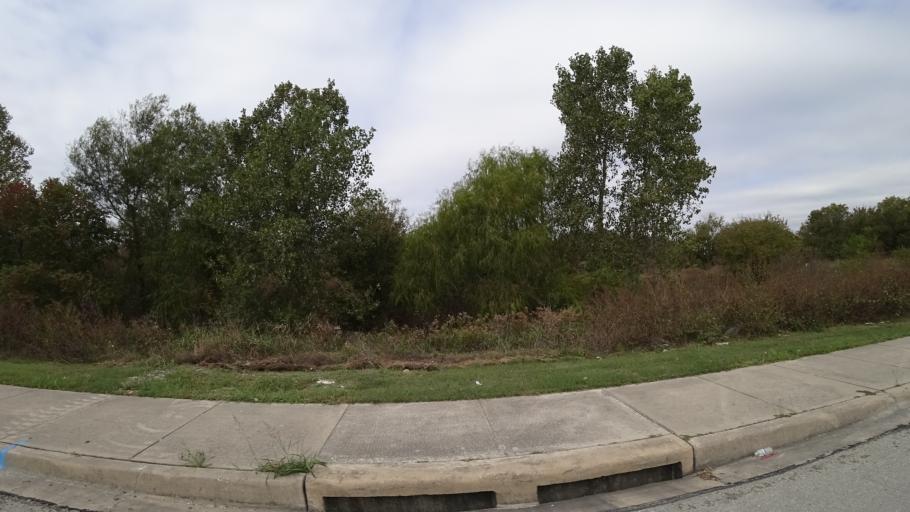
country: US
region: Texas
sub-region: Travis County
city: Windemere
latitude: 30.4630
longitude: -97.6467
